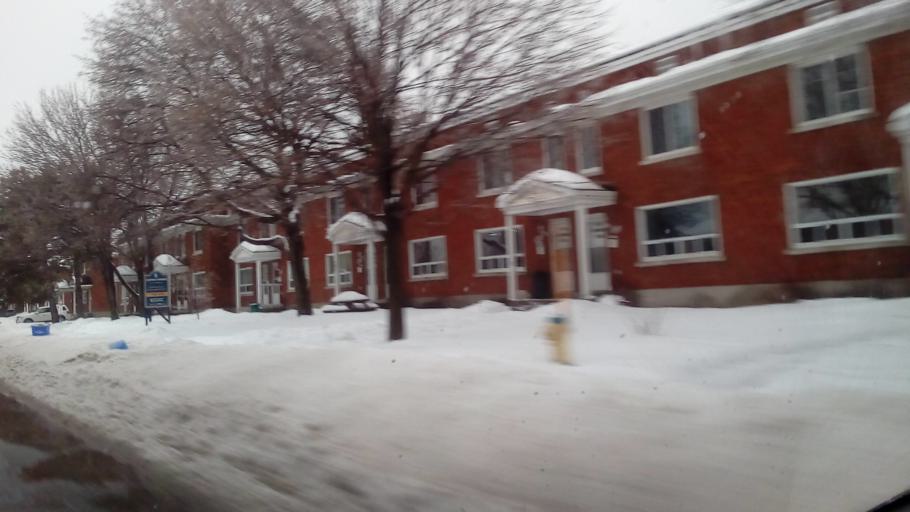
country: CA
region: Ontario
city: Ottawa
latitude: 45.4369
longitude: -75.6375
